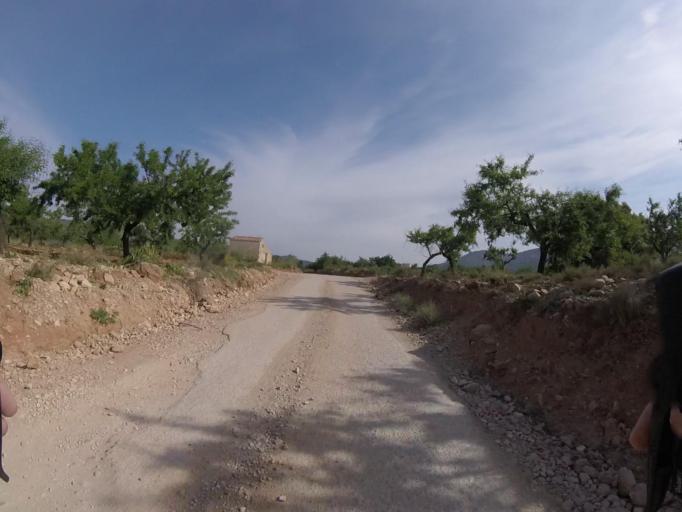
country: ES
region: Valencia
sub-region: Provincia de Castello
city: Alcoceber
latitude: 40.2739
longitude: 0.2579
